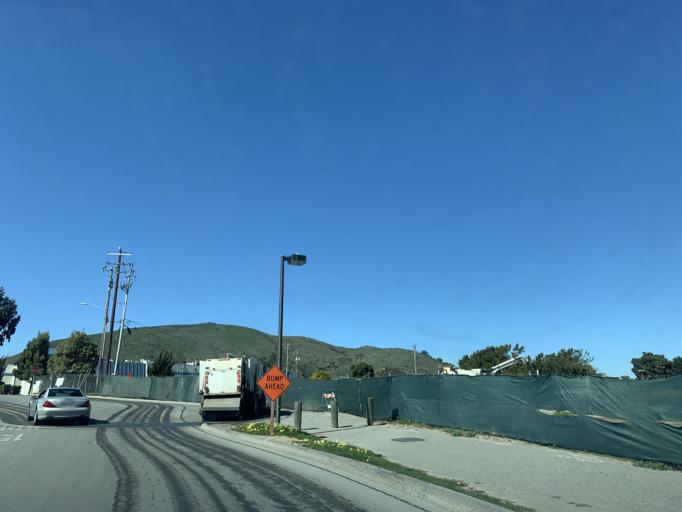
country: US
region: California
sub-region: San Mateo County
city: Brisbane
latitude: 37.6638
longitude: -122.3837
